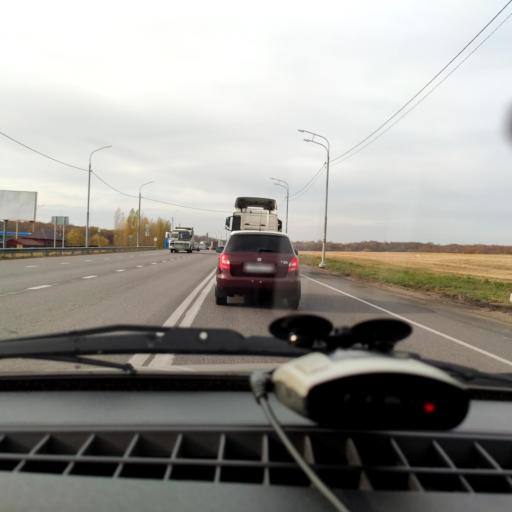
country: RU
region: Voronezj
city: Semiluki
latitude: 51.6525
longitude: 39.0418
